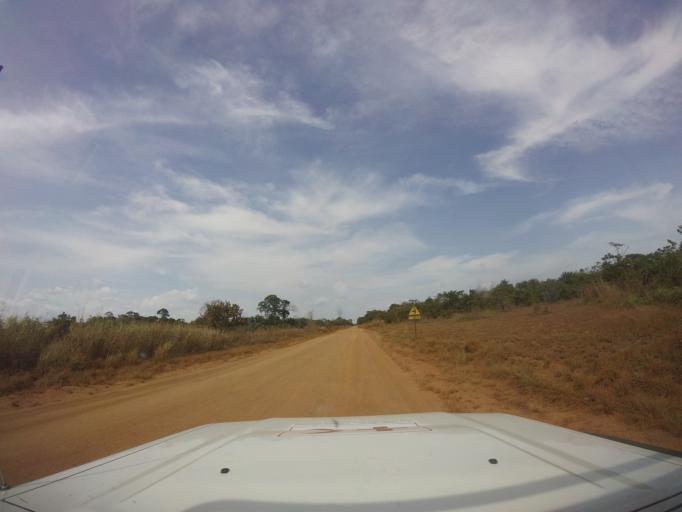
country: LR
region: Grand Cape Mount
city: Robertsport
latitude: 6.6855
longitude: -11.1236
